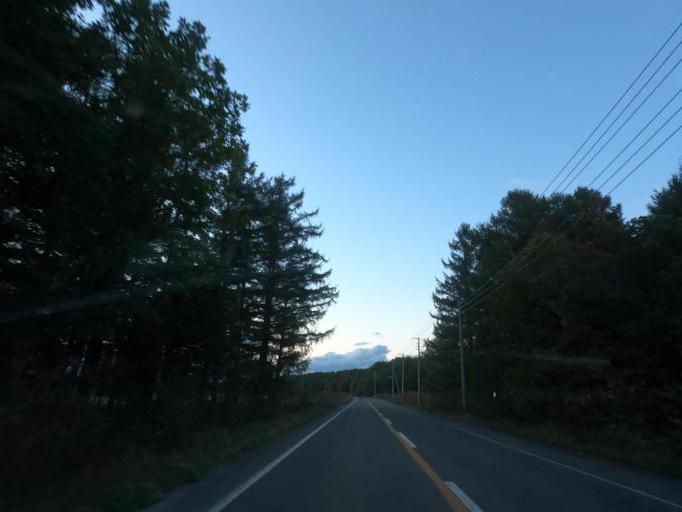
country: JP
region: Hokkaido
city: Obihiro
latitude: 42.6741
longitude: 143.1671
